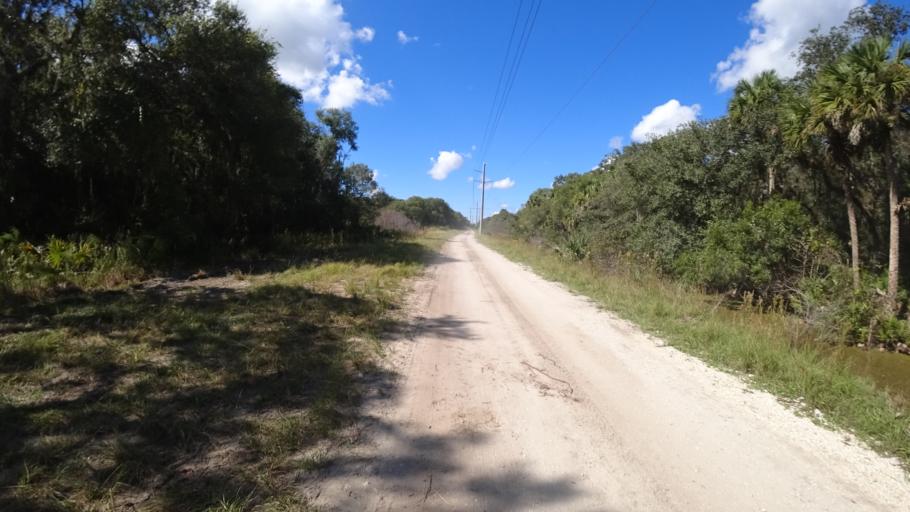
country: US
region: Florida
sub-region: Sarasota County
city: Lake Sarasota
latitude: 27.2501
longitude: -82.2918
